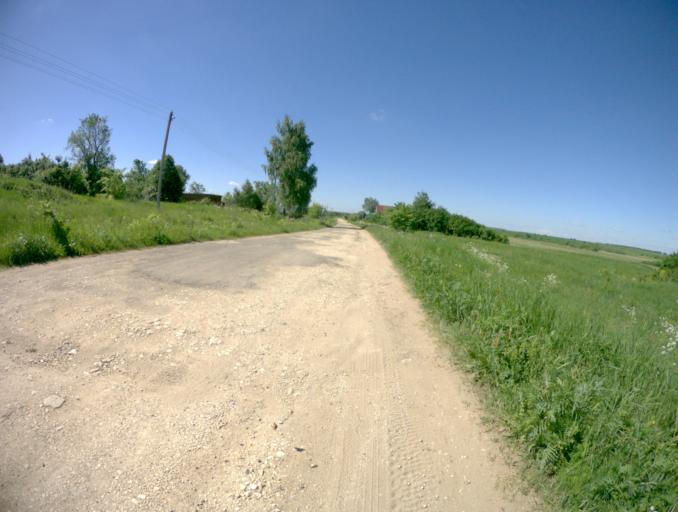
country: RU
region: Ivanovo
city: Gavrilov Posad
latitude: 56.5218
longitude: 40.2167
